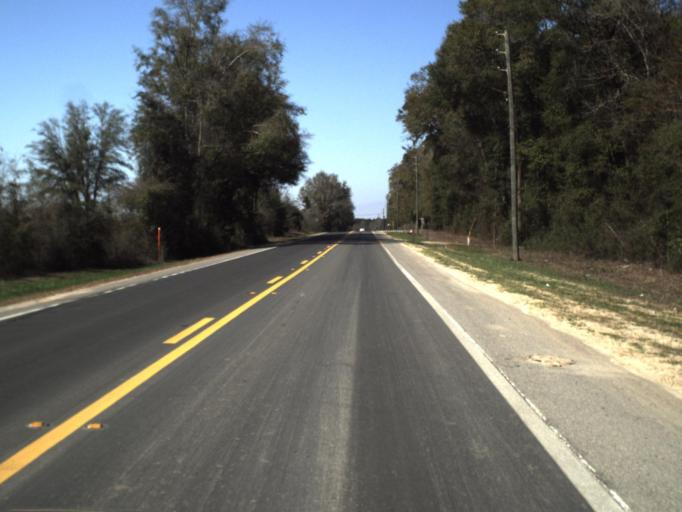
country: US
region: Florida
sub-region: Jackson County
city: Marianna
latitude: 30.6377
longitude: -85.1578
